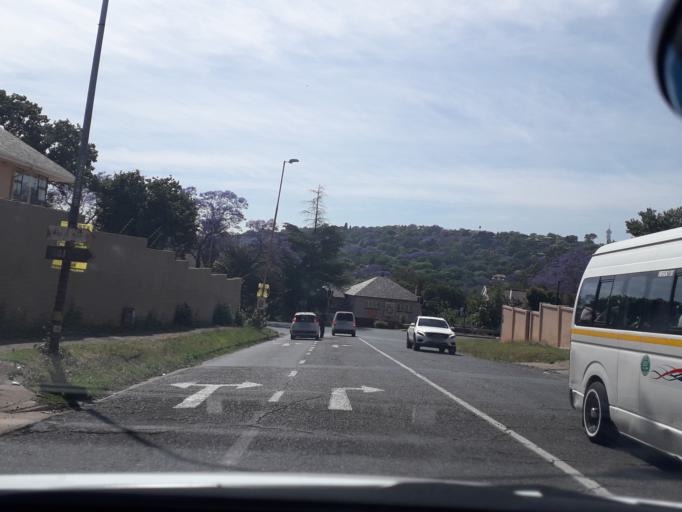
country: ZA
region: Gauteng
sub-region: City of Johannesburg Metropolitan Municipality
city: Johannesburg
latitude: -26.1678
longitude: 28.0134
